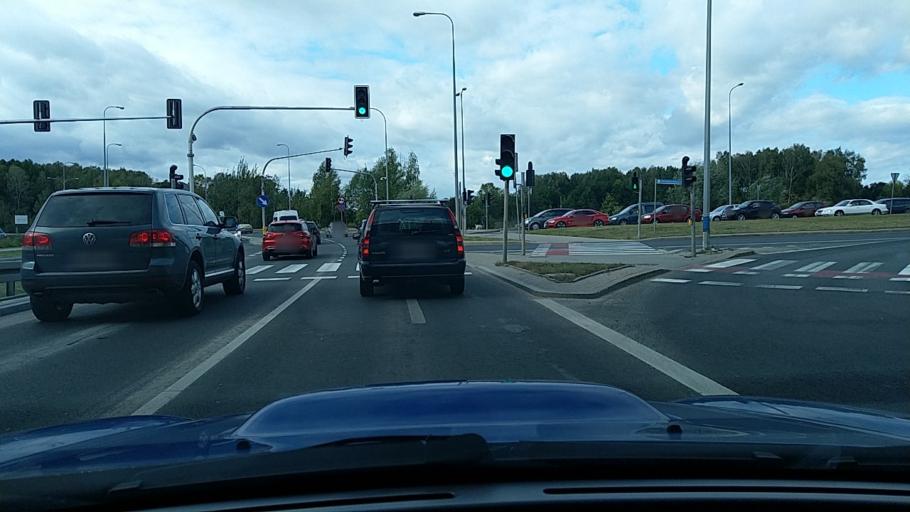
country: PL
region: Warmian-Masurian Voivodeship
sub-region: Olsztyn
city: Kortowo
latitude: 53.7741
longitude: 20.4547
